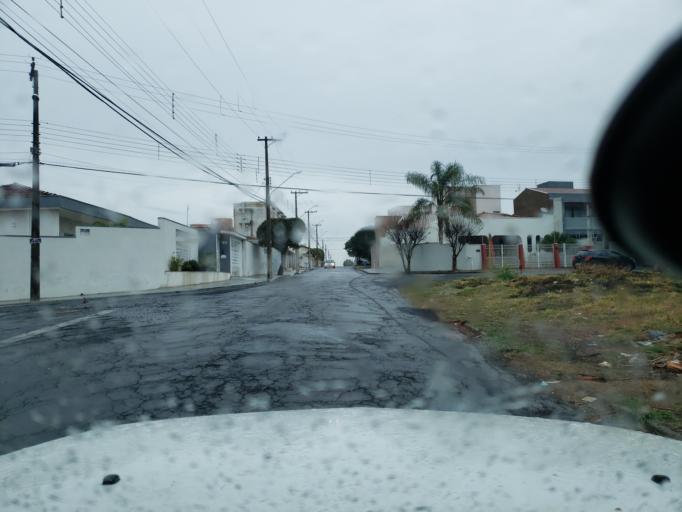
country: BR
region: Sao Paulo
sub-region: Moji-Guacu
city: Mogi-Gaucu
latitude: -22.3804
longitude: -46.9359
